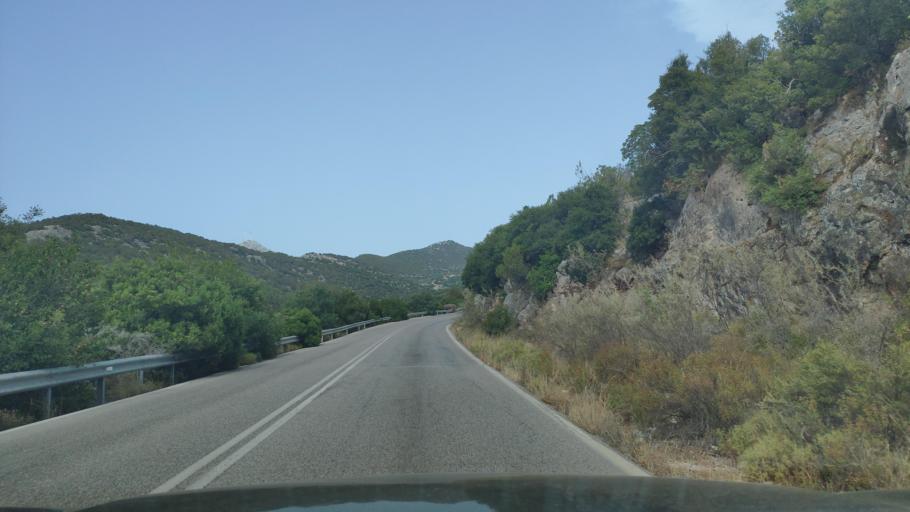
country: GR
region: Peloponnese
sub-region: Nomos Argolidos
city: Didyma
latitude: 37.5110
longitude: 23.1896
